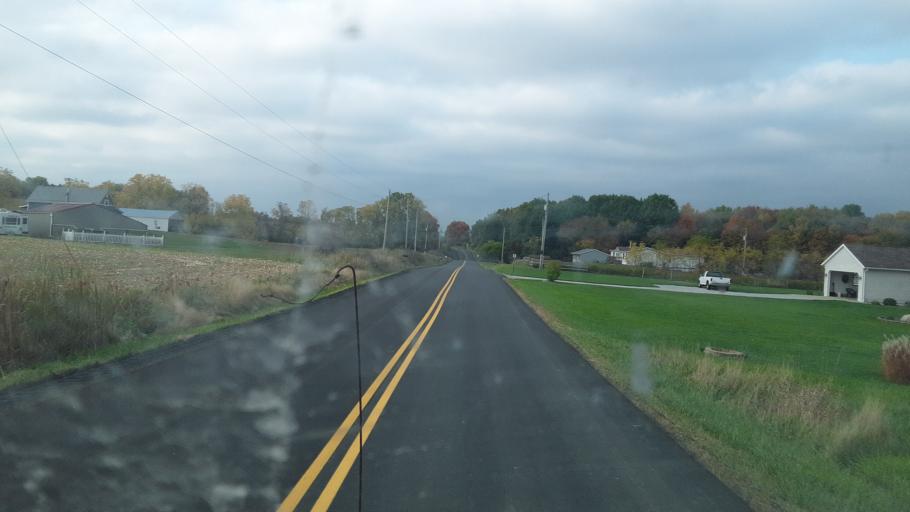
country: US
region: Ohio
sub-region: Ashland County
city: Loudonville
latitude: 40.7585
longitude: -82.2228
